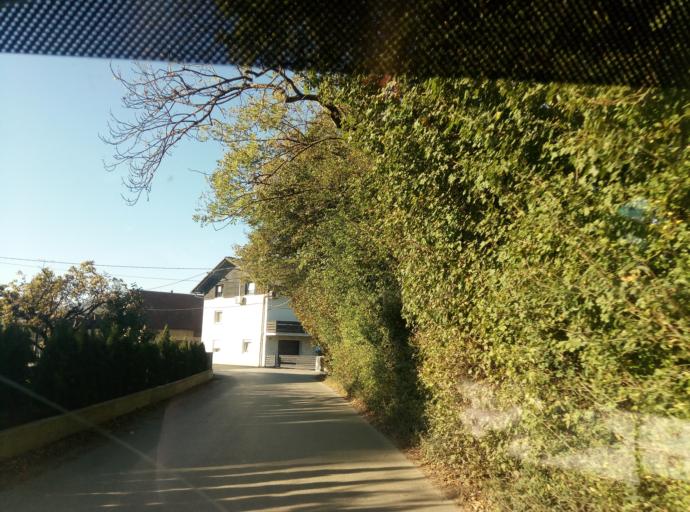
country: SI
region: Ljubljana
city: Ljubljana
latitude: 46.0979
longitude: 14.5027
